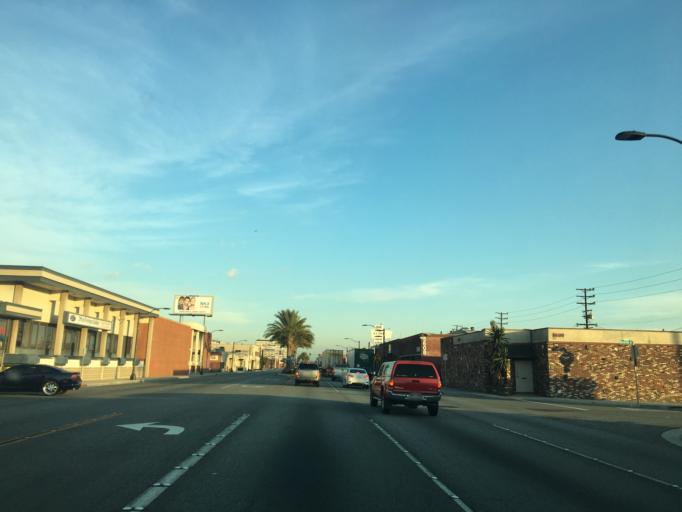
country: US
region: California
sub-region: Los Angeles County
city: Commerce
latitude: 34.0000
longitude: -118.1587
